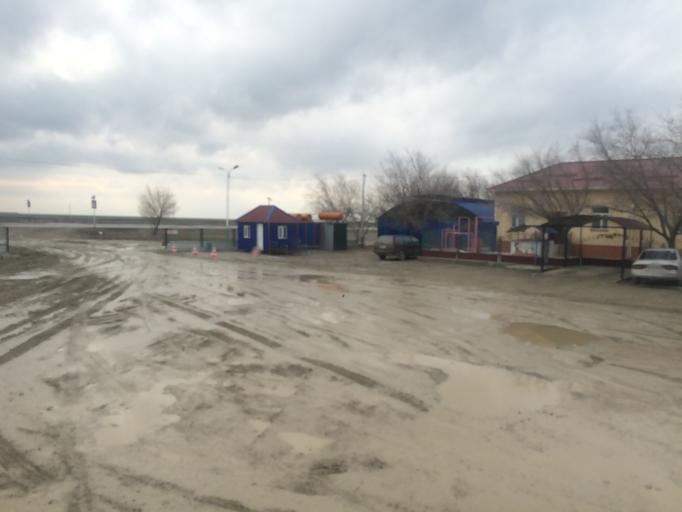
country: KZ
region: Qyzylorda
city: Shalqiya
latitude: 43.6059
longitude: 67.6726
